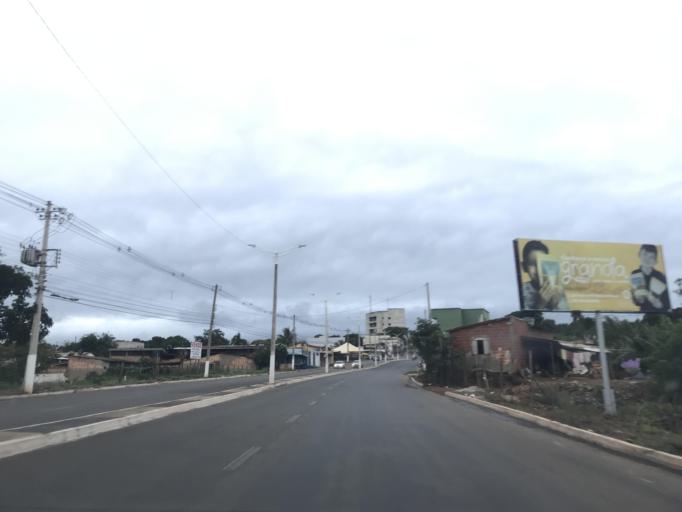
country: BR
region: Goias
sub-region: Luziania
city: Luziania
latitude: -16.2434
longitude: -47.9454
